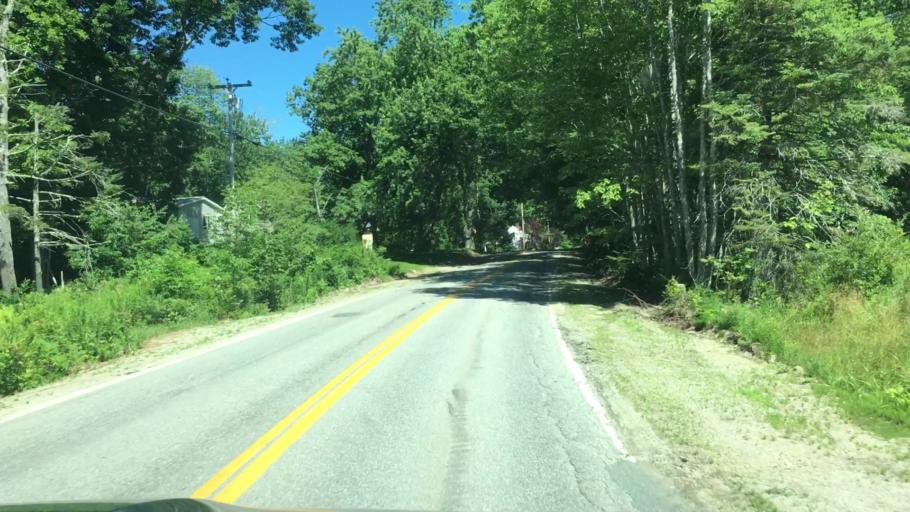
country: US
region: Maine
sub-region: Hancock County
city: Penobscot
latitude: 44.4581
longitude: -68.7049
